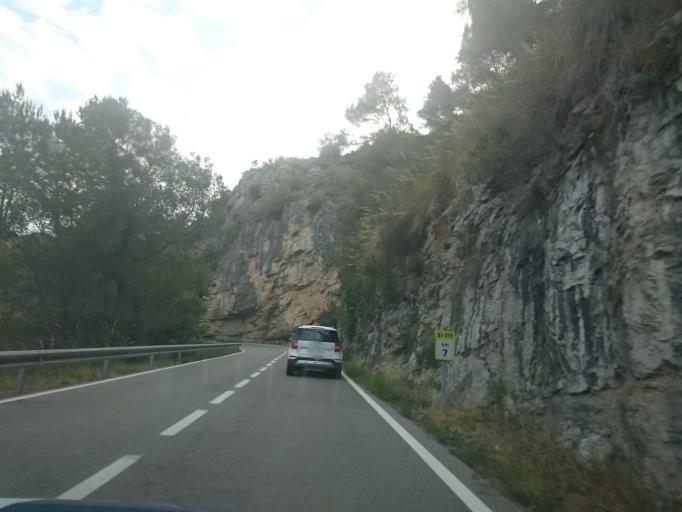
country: ES
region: Catalonia
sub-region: Provincia de Barcelona
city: Castellet
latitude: 41.2453
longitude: 1.6642
